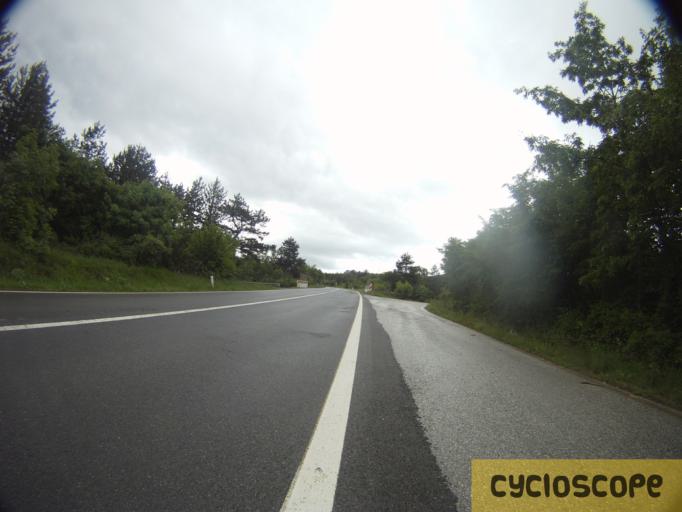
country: SI
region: Divaca
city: Divaca
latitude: 45.6455
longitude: 13.9615
